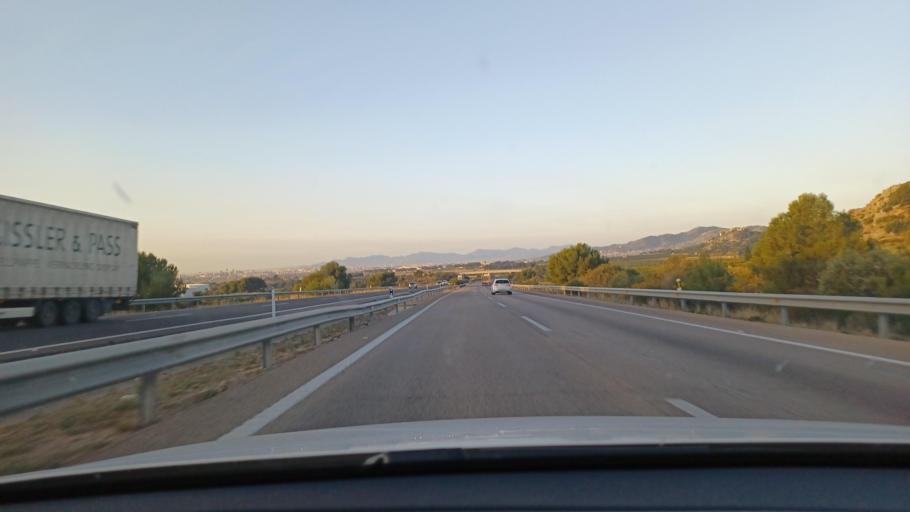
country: ES
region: Valencia
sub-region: Provincia de Castello
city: Benicassim
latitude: 40.0385
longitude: 0.0172
